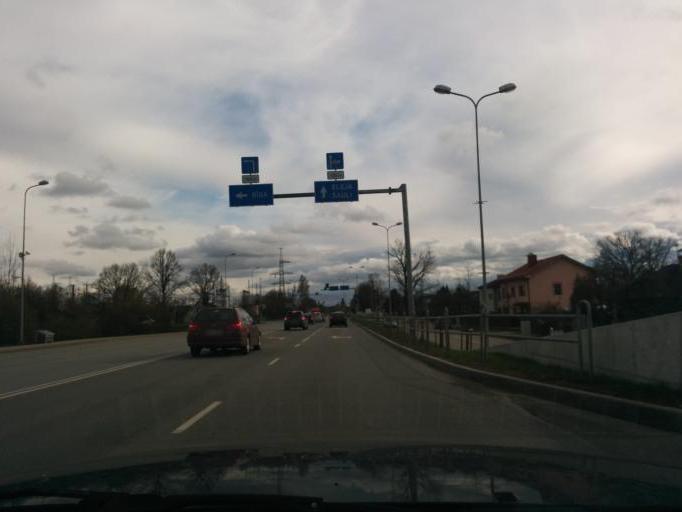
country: LV
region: Jelgava
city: Jelgava
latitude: 56.6314
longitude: 23.7267
